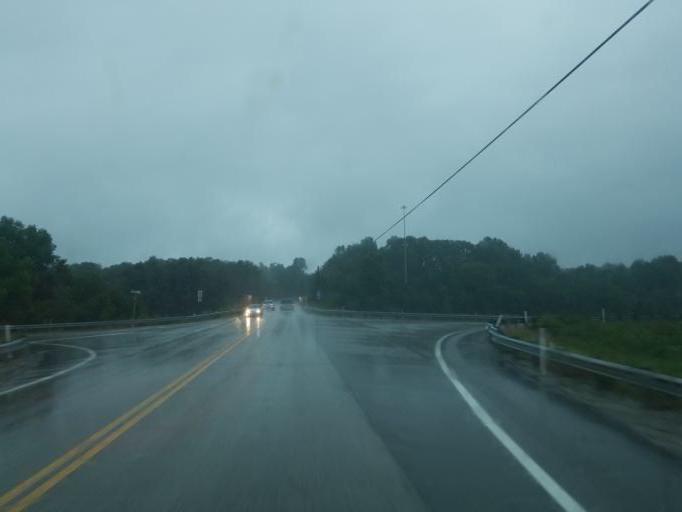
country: US
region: Kentucky
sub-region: Carter County
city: Olive Hill
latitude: 38.3300
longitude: -83.2089
